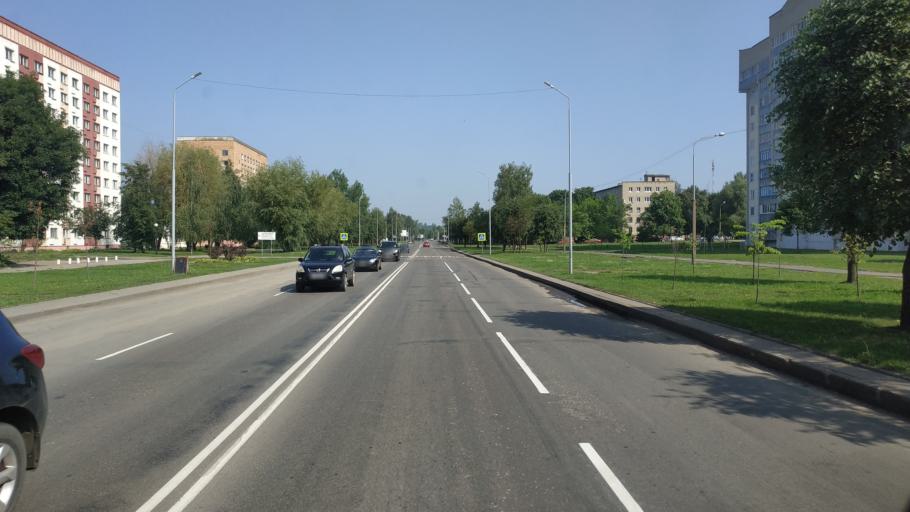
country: BY
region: Mogilev
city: Buynichy
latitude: 53.8692
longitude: 30.3137
